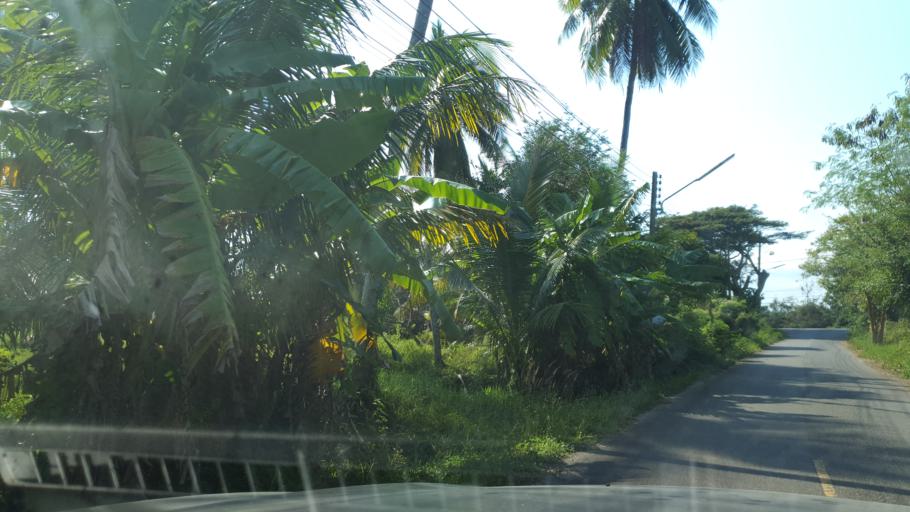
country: TH
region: Prachuap Khiri Khan
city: Thap Sakae
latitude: 11.3620
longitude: 99.5529
